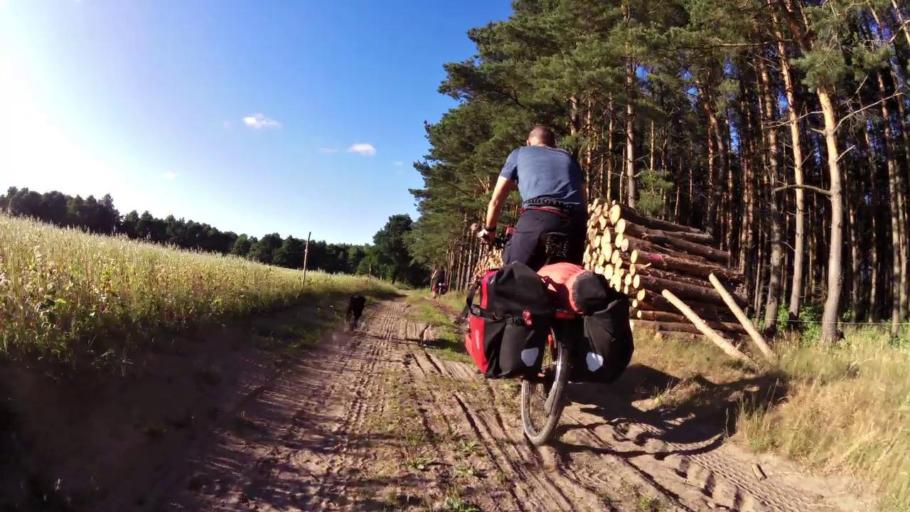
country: PL
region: West Pomeranian Voivodeship
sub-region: Powiat swidwinski
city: Swidwin
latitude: 53.7145
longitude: 15.8319
